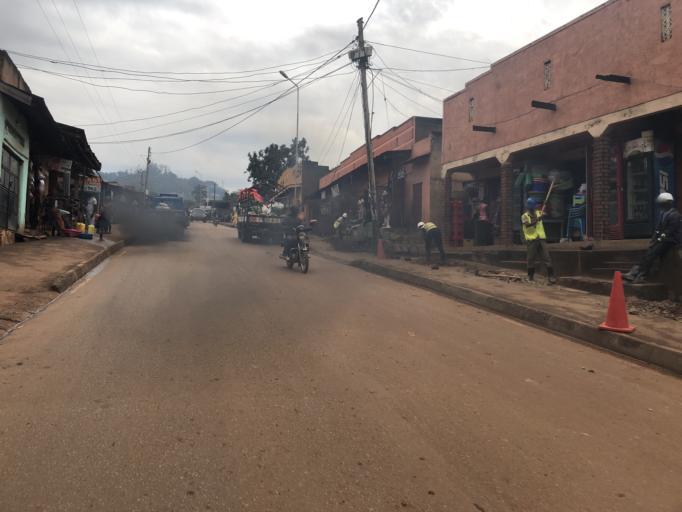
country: UG
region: Central Region
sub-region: Kampala District
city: Kampala
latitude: 0.2820
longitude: 32.6027
